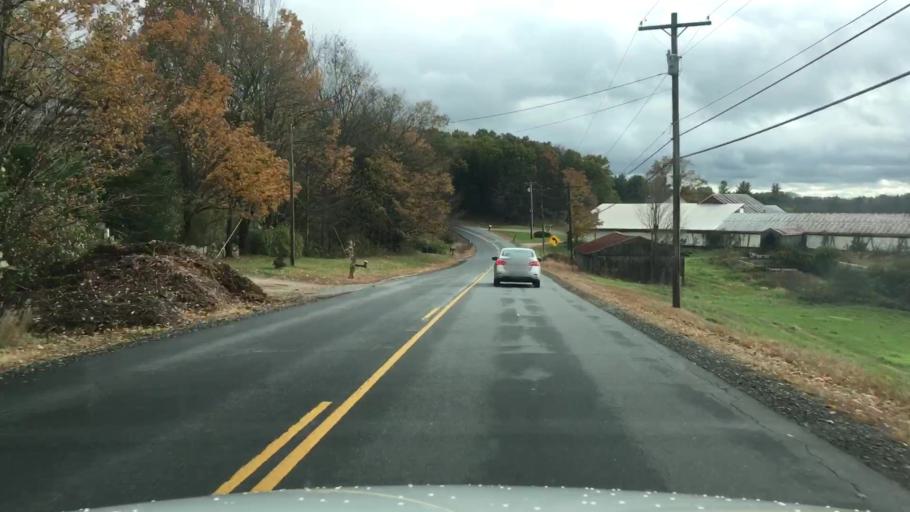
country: US
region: New Hampshire
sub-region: Strafford County
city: Lee
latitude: 43.0918
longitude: -70.9825
